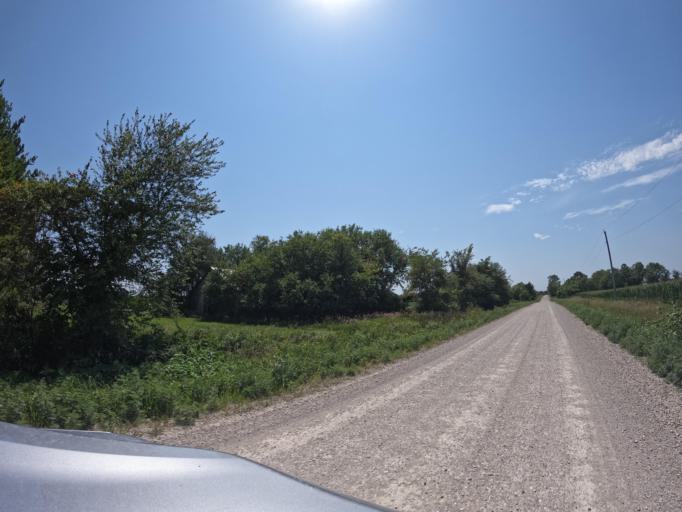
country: US
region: Iowa
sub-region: Henry County
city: Mount Pleasant
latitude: 40.8903
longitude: -91.6408
